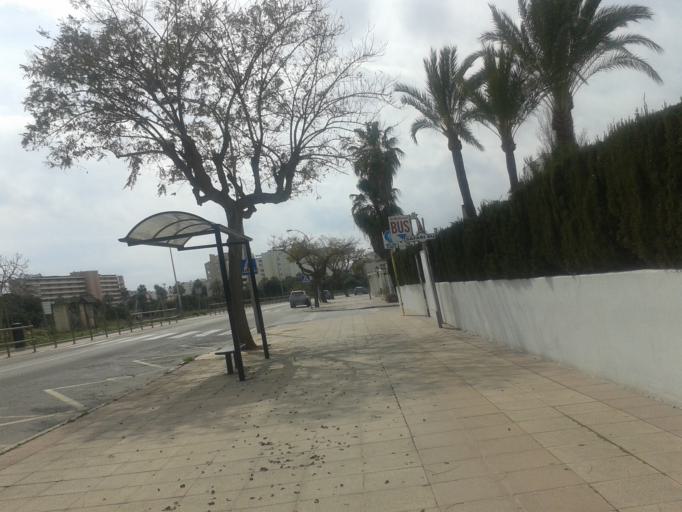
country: ES
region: Balearic Islands
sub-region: Illes Balears
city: Son Servera
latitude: 39.5801
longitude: 3.3786
